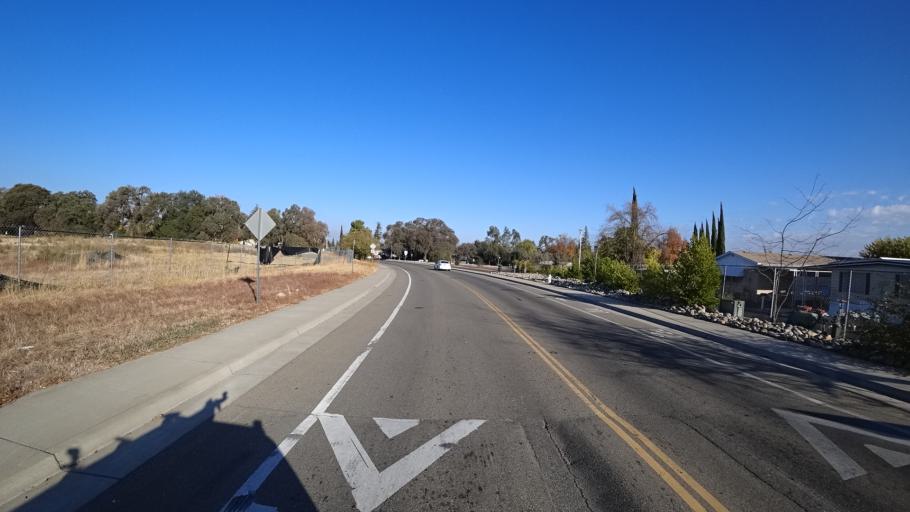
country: US
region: California
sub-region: Sacramento County
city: Citrus Heights
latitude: 38.7105
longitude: -121.2537
